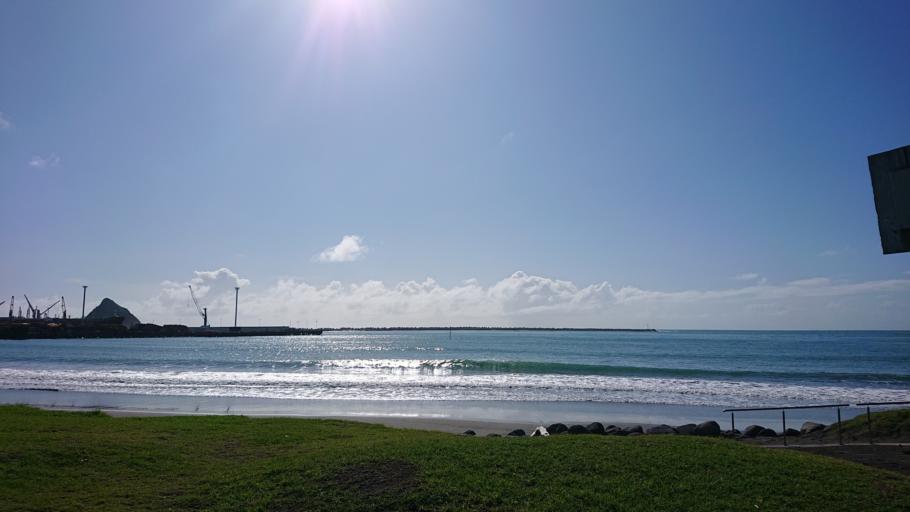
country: NZ
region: Taranaki
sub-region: New Plymouth District
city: New Plymouth
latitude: -39.0609
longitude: 174.0411
